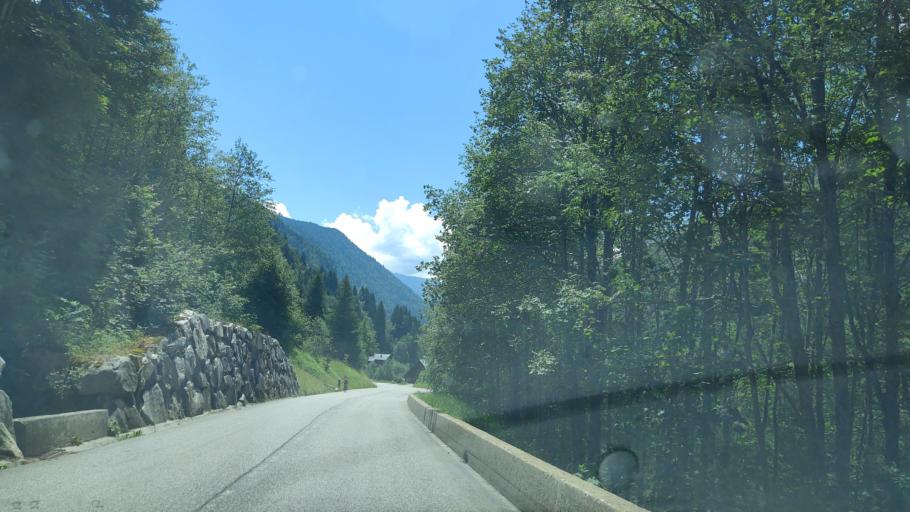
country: FR
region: Rhone-Alpes
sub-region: Departement de la Haute-Savoie
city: Praz-sur-Arly
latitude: 45.8579
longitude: 6.4979
